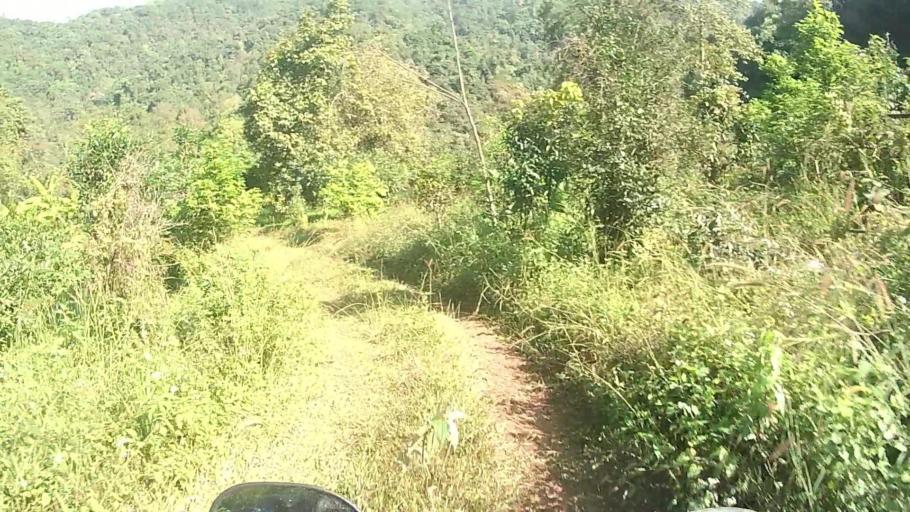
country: TH
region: Chiang Mai
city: Mae On
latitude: 19.0501
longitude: 99.2898
